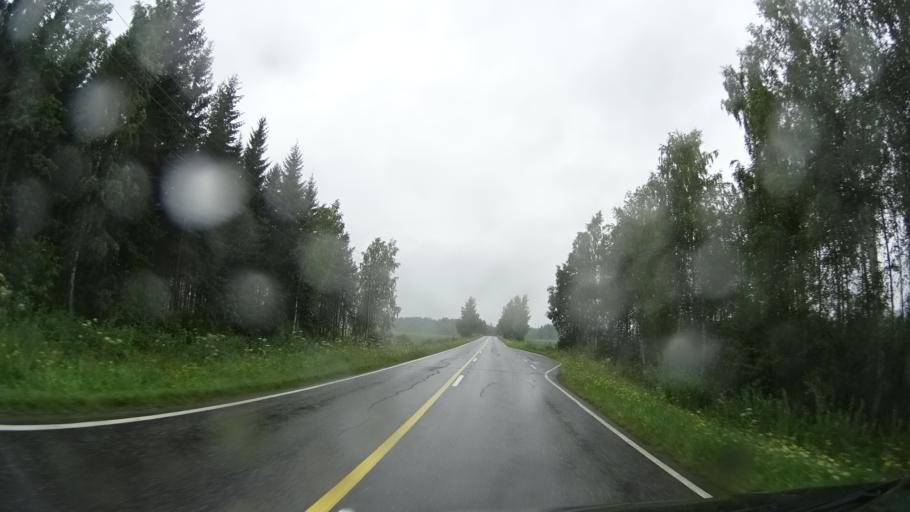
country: FI
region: North Karelia
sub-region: Keski-Karjala
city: Raeaekkylae
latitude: 62.3060
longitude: 29.5410
